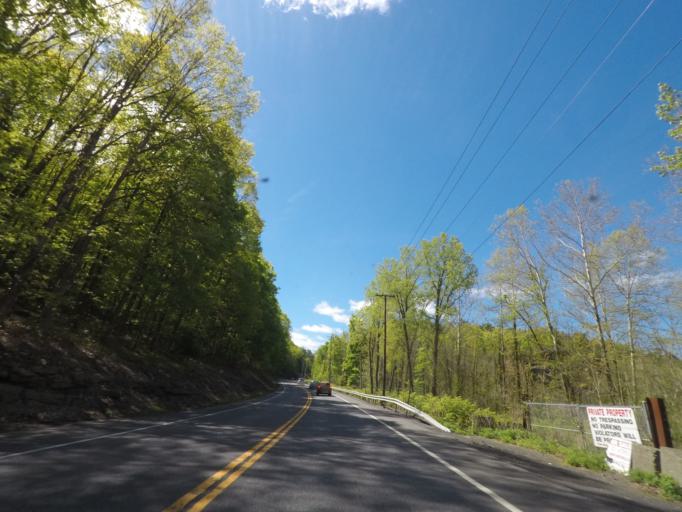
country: US
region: New York
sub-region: Ulster County
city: Glasco
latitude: 42.0218
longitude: -73.9776
